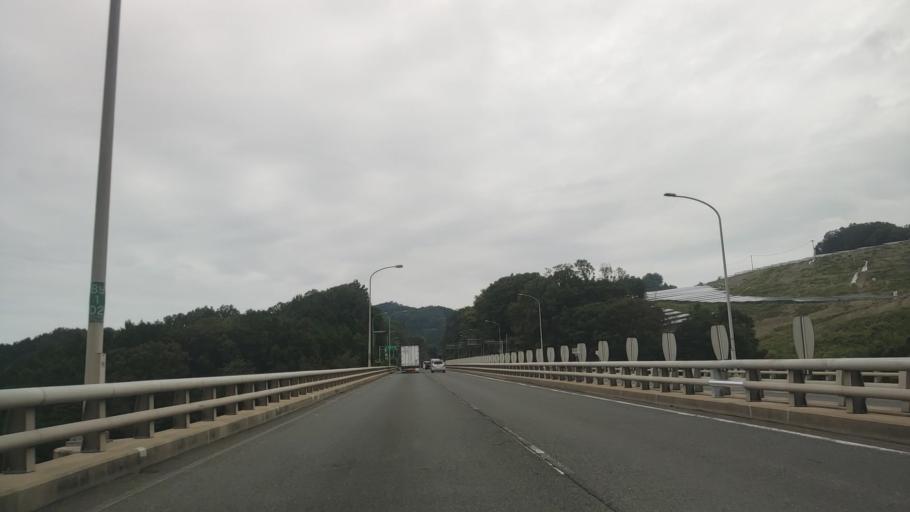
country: JP
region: Nara
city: Tenri
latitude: 34.6239
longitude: 135.8808
